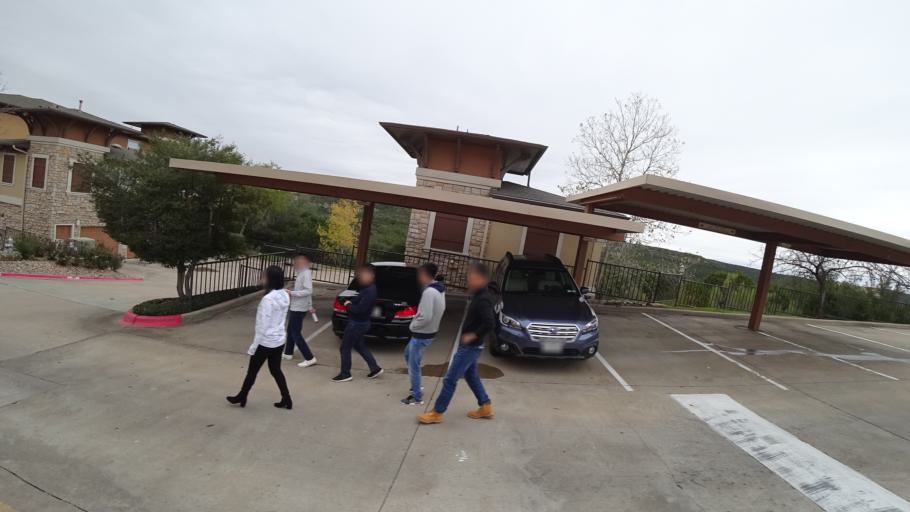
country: US
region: Texas
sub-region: Travis County
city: West Lake Hills
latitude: 30.3651
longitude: -97.7928
